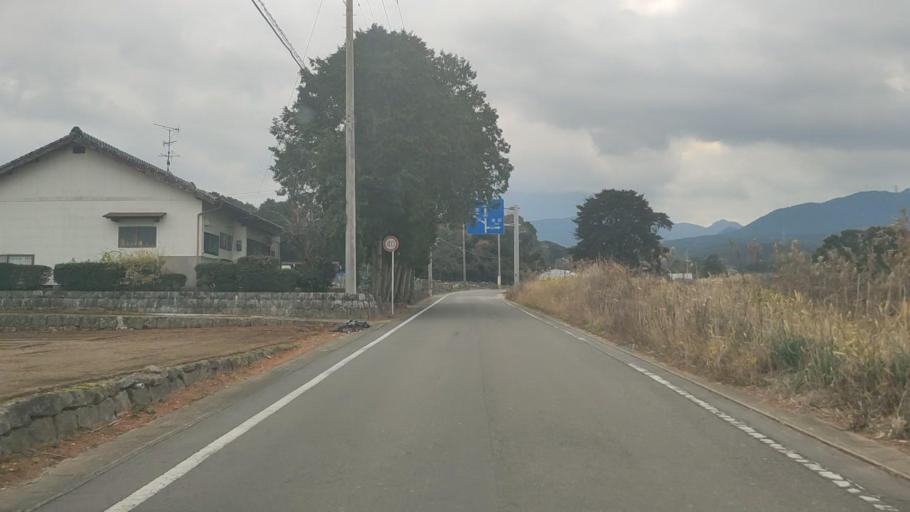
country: JP
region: Nagasaki
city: Shimabara
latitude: 32.8283
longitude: 130.2919
